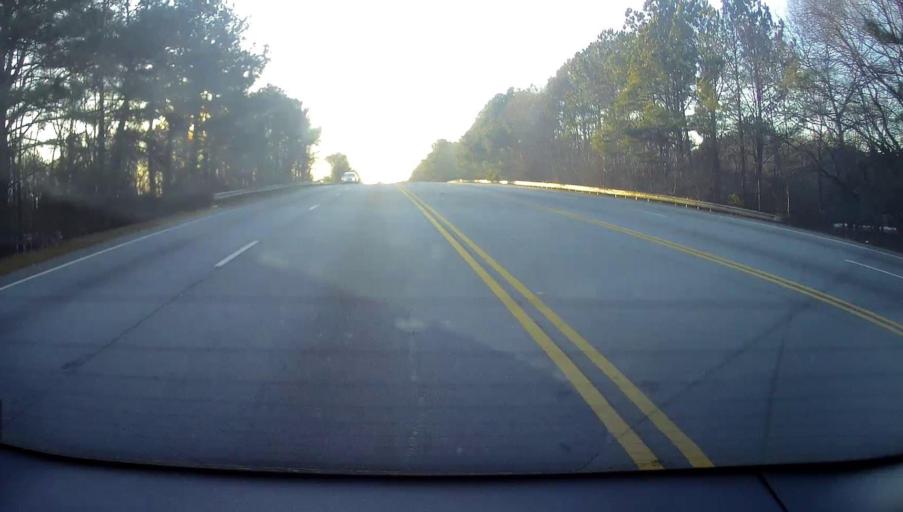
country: US
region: Georgia
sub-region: Fulton County
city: Union City
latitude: 33.5704
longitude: -84.5483
